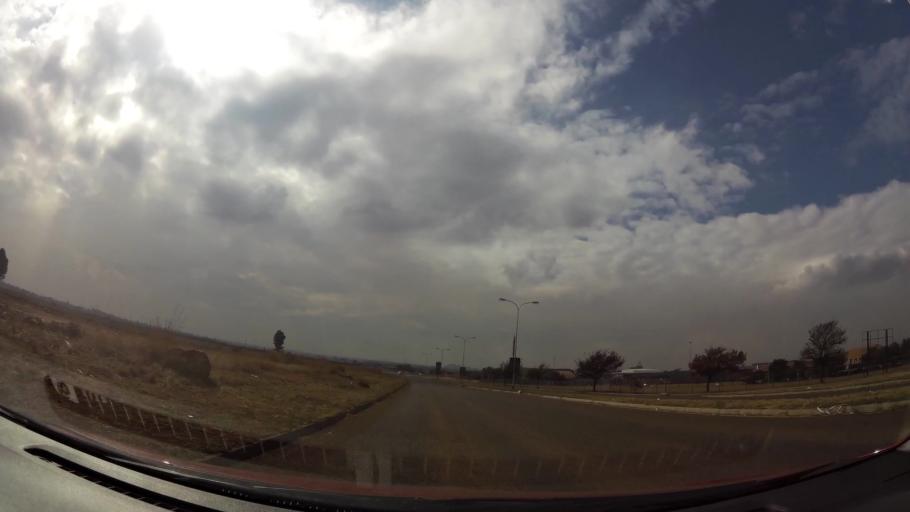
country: ZA
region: Gauteng
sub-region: Sedibeng District Municipality
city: Vanderbijlpark
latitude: -26.7259
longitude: 27.8772
